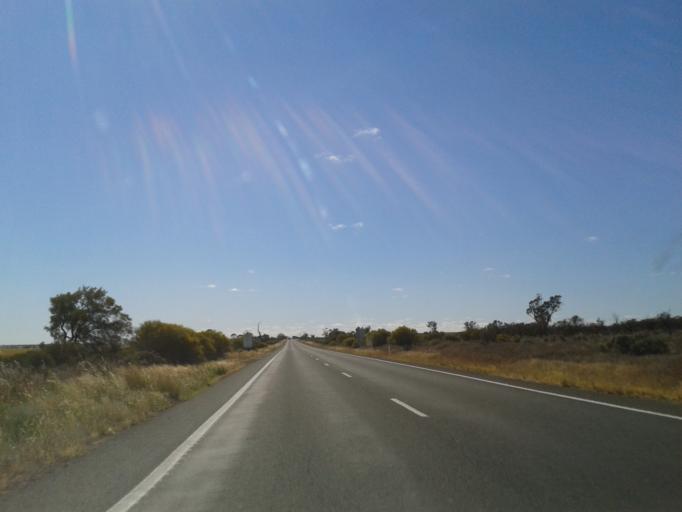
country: AU
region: New South Wales
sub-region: Wentworth
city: Dareton
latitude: -34.2762
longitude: 141.4269
